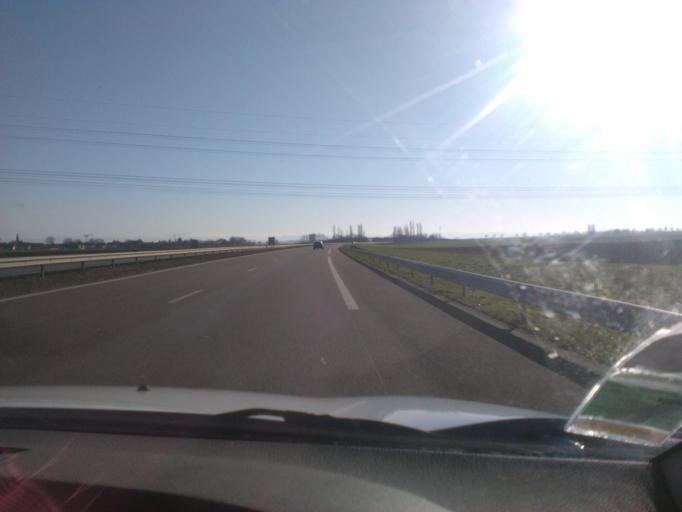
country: FR
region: Alsace
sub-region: Departement du Bas-Rhin
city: Altorf
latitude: 48.5197
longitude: 7.5121
